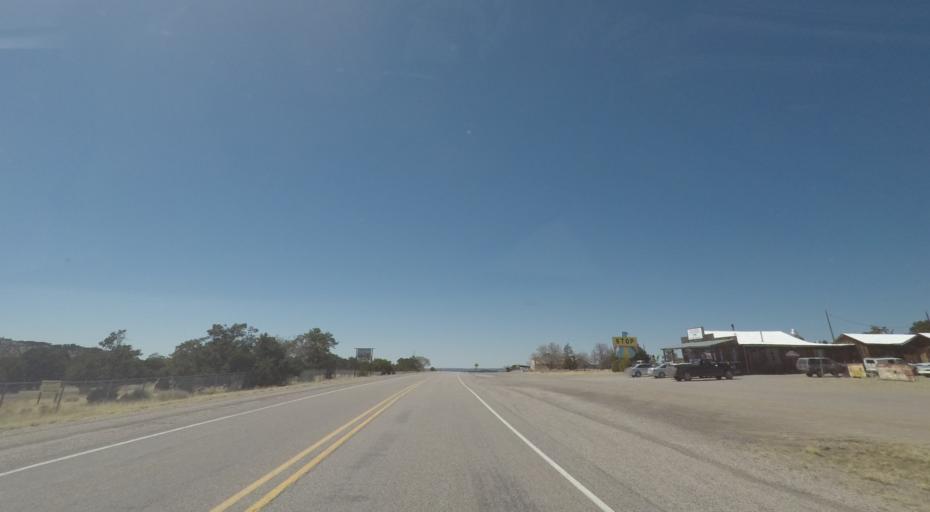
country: US
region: New Mexico
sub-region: Socorro County
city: Alamo
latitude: 34.2987
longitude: -108.1298
